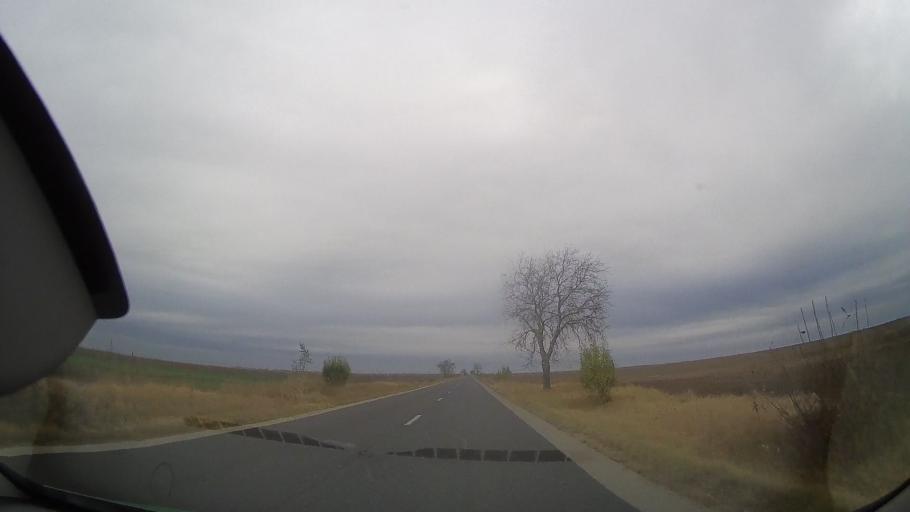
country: RO
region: Ialomita
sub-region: Comuna Milosesti
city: Milosesti
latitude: 44.7709
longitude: 27.1817
